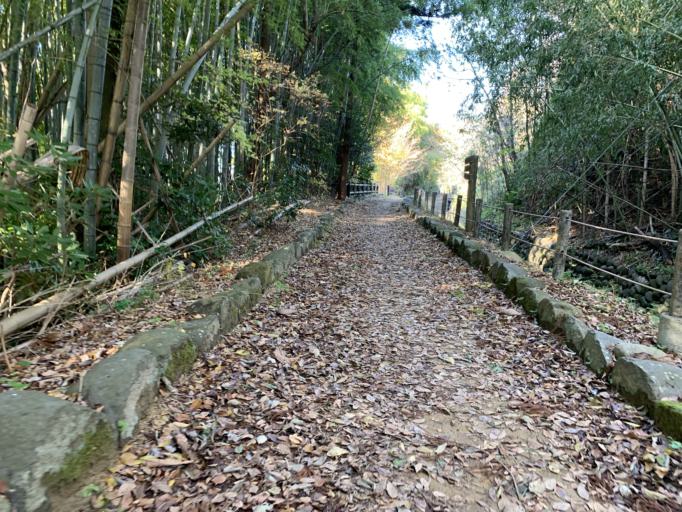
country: JP
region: Ishikawa
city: Nonoichi
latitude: 36.5346
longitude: 136.6884
